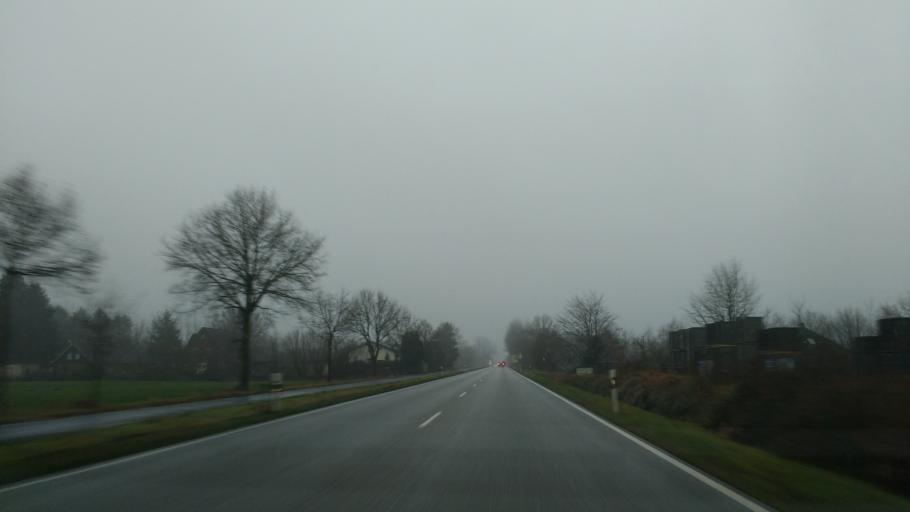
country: DE
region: Schleswig-Holstein
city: Brinjahe
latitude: 54.1878
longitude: 9.6398
